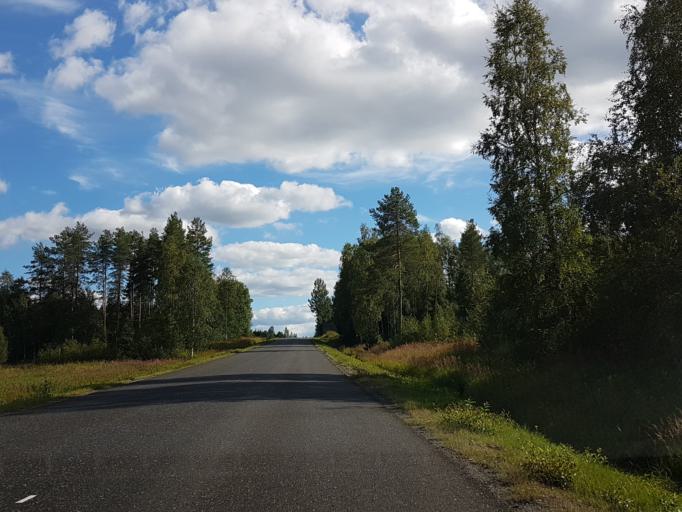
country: SE
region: Vaesterbotten
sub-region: Skelleftea Kommun
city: Burtraesk
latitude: 64.2899
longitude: 20.5245
